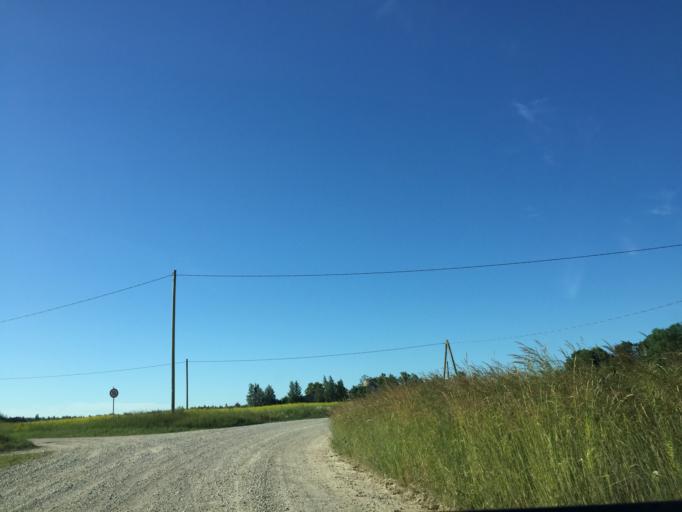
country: LV
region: Ventspils Rajons
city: Piltene
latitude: 57.3241
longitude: 21.6891
